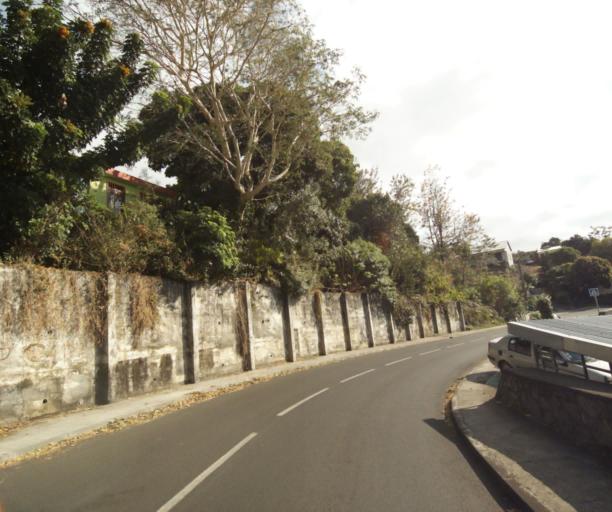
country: RE
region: Reunion
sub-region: Reunion
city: Saint-Paul
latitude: -21.0078
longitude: 55.3214
